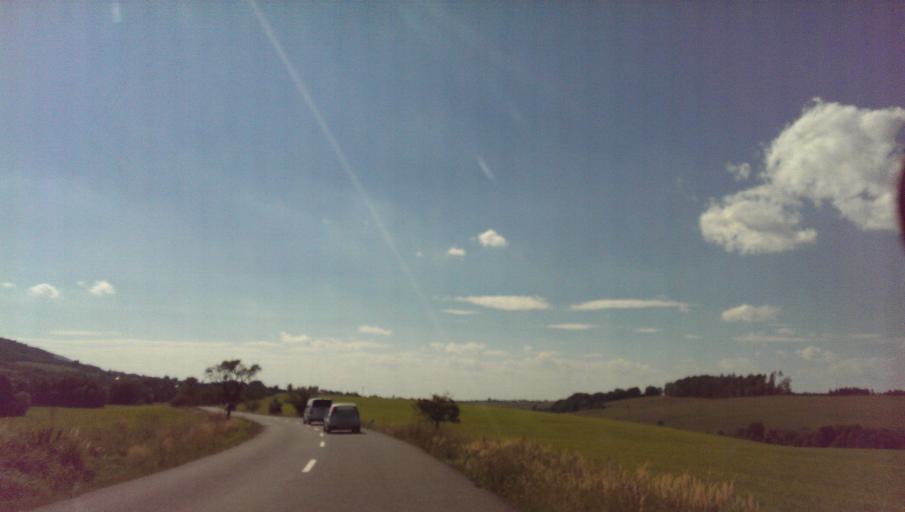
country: CZ
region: Zlin
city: Kelc
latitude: 49.4446
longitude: 17.8552
